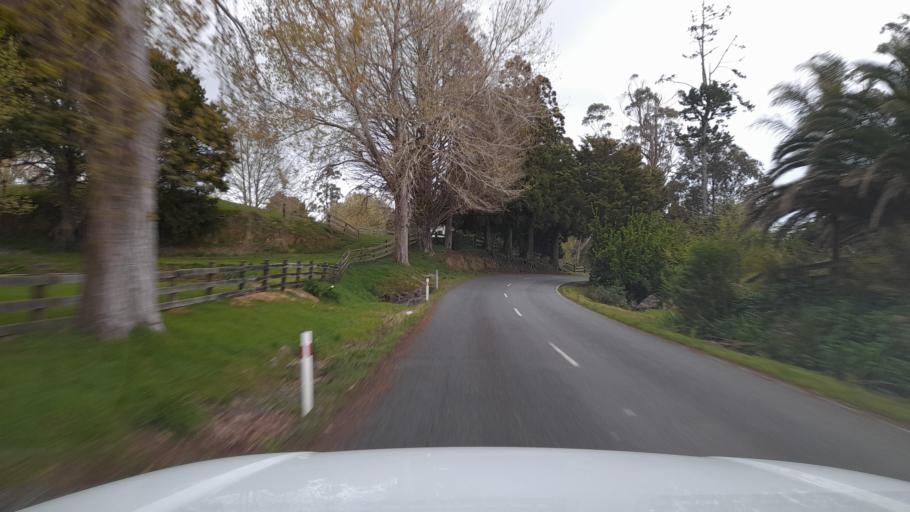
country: NZ
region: Northland
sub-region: Whangarei
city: Maungatapere
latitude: -35.6390
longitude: 174.2078
